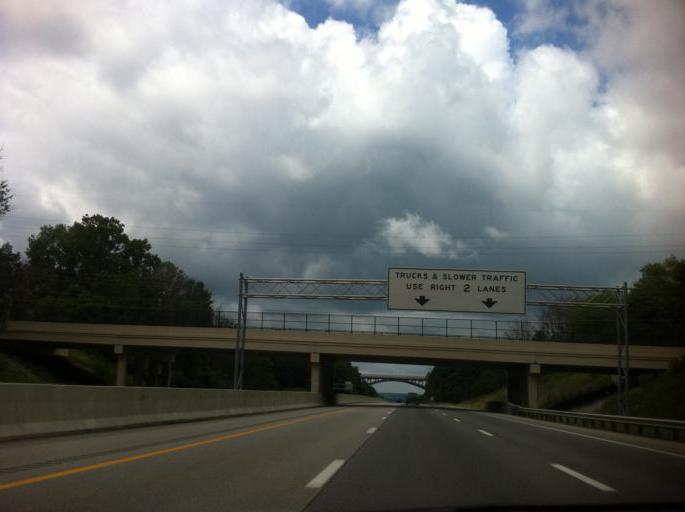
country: US
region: Ohio
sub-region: Summit County
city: Boston Heights
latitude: 41.2586
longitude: -81.5034
